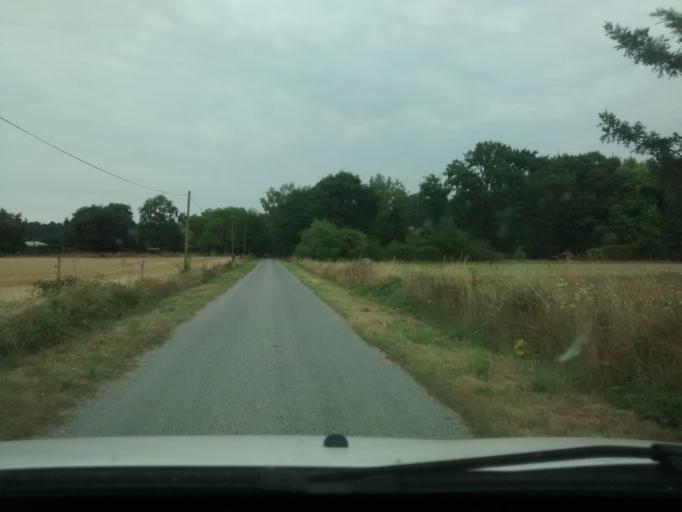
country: FR
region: Brittany
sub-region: Departement d'Ille-et-Vilaine
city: Cesson-Sevigne
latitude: 48.1009
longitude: -1.5954
